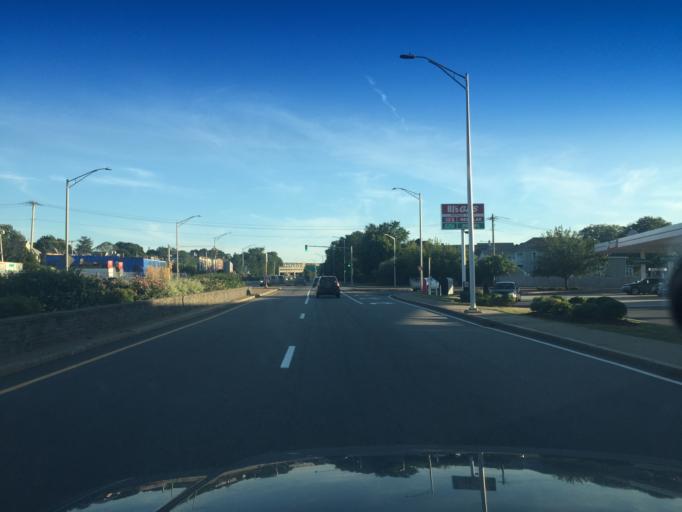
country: US
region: Massachusetts
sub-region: Norfolk County
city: Quincy
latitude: 42.2399
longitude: -71.0056
